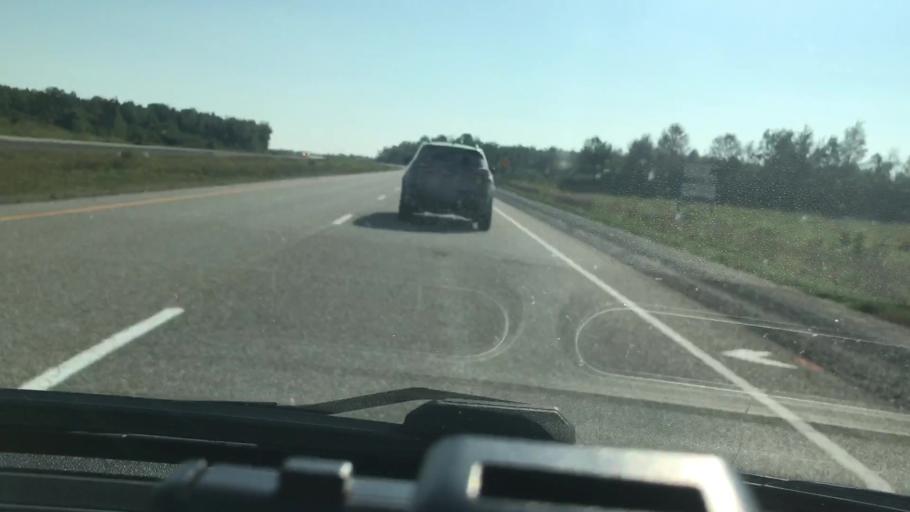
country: CA
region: Ontario
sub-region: Algoma
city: Sault Ste. Marie
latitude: 46.4774
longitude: -84.0536
